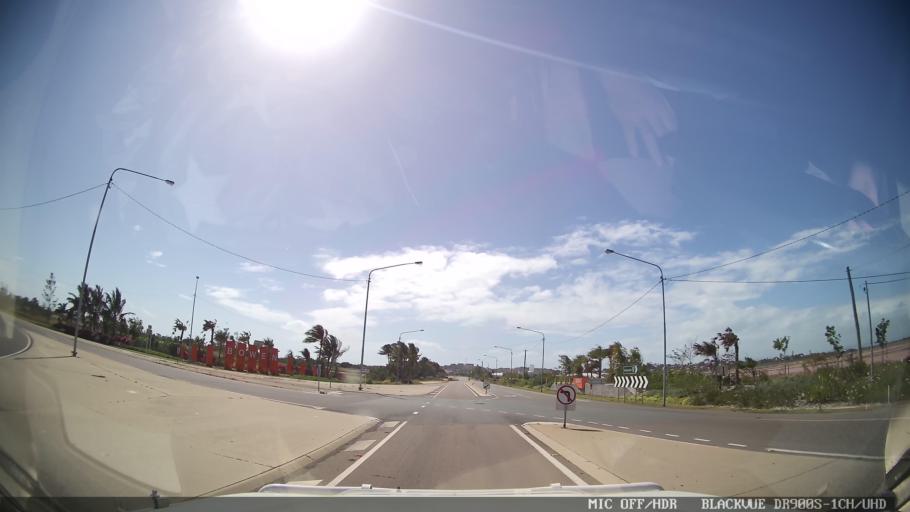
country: AU
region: Queensland
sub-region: Whitsunday
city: Bowen
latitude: -20.0153
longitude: 148.2212
